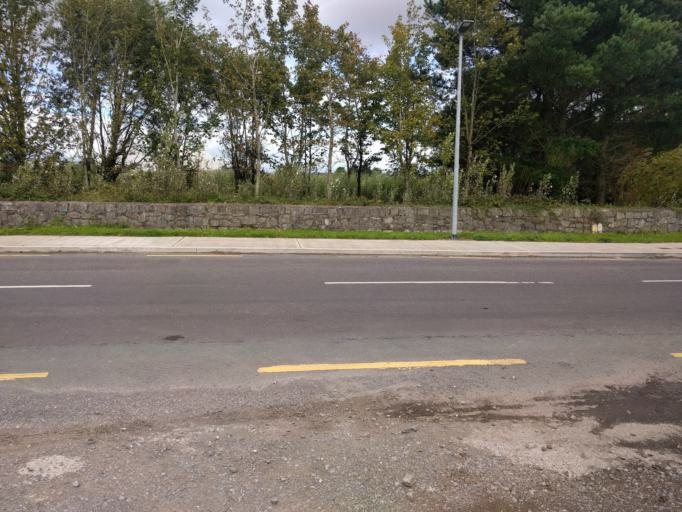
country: IE
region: Munster
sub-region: County Cork
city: Cobh
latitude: 51.8310
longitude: -8.3031
